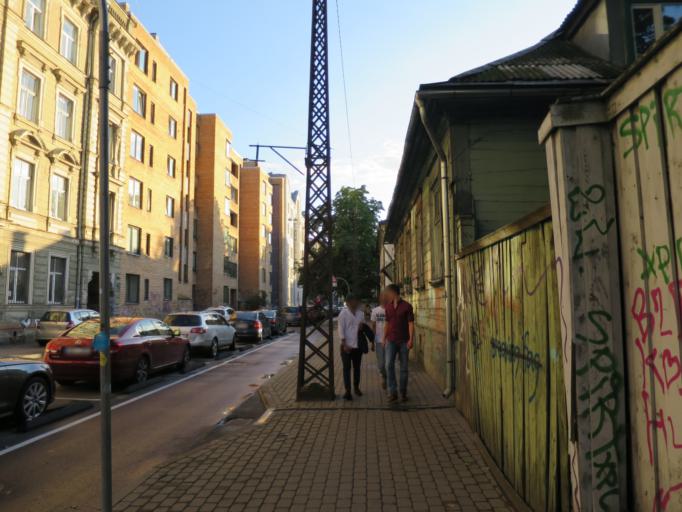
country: LV
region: Riga
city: Riga
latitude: 56.9606
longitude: 24.1235
